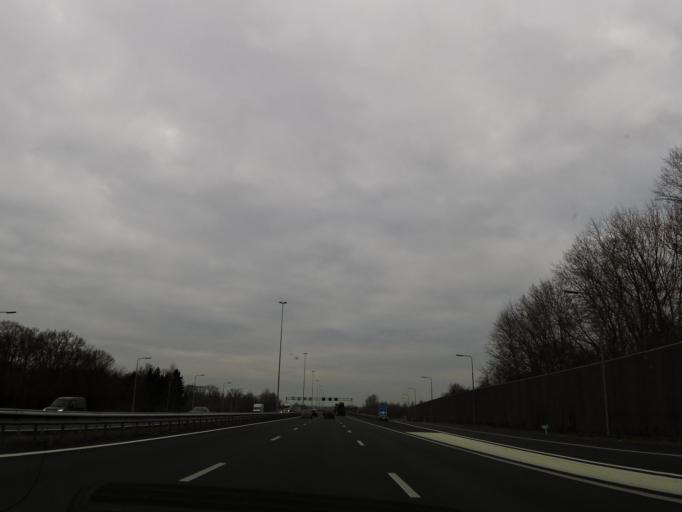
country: NL
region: North Brabant
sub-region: Gemeente Boxtel
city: Boxtel
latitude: 51.5733
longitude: 5.3565
